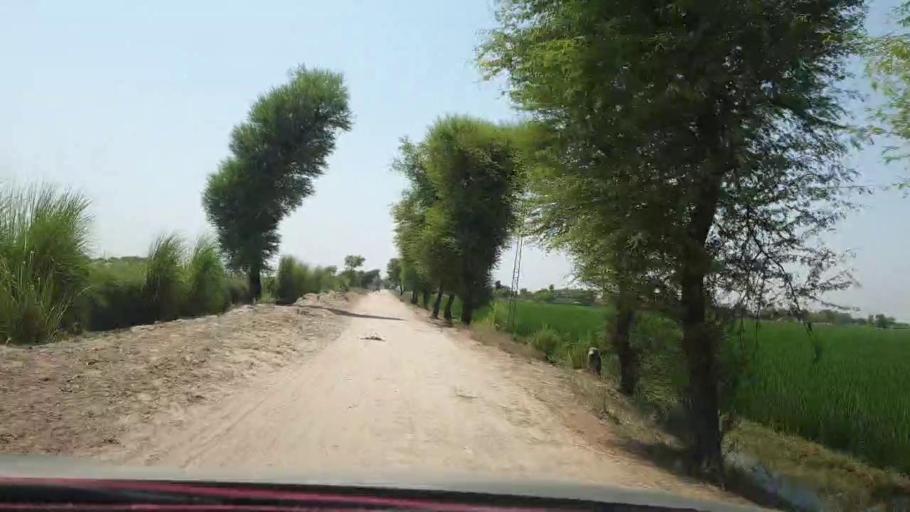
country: PK
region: Sindh
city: Warah
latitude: 27.5028
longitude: 67.7827
